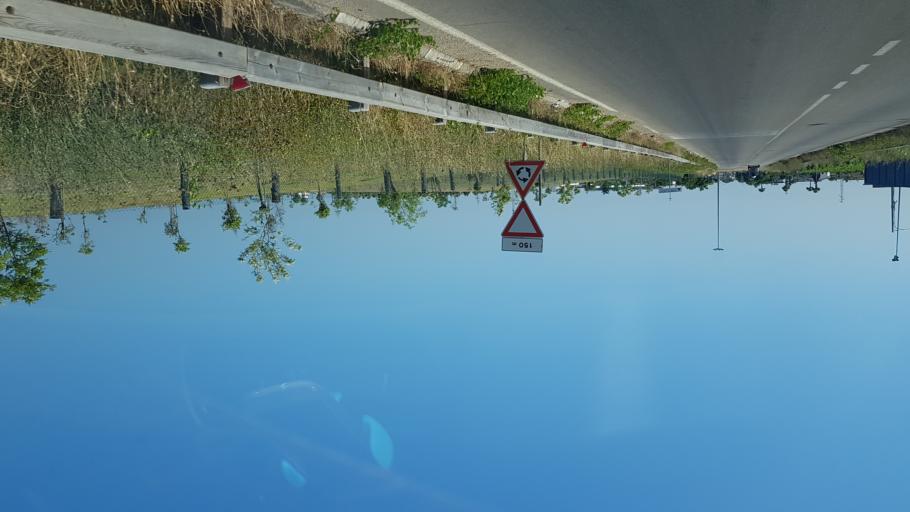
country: IT
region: Apulia
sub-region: Provincia di Lecce
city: Veglie
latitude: 40.3516
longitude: 17.9686
